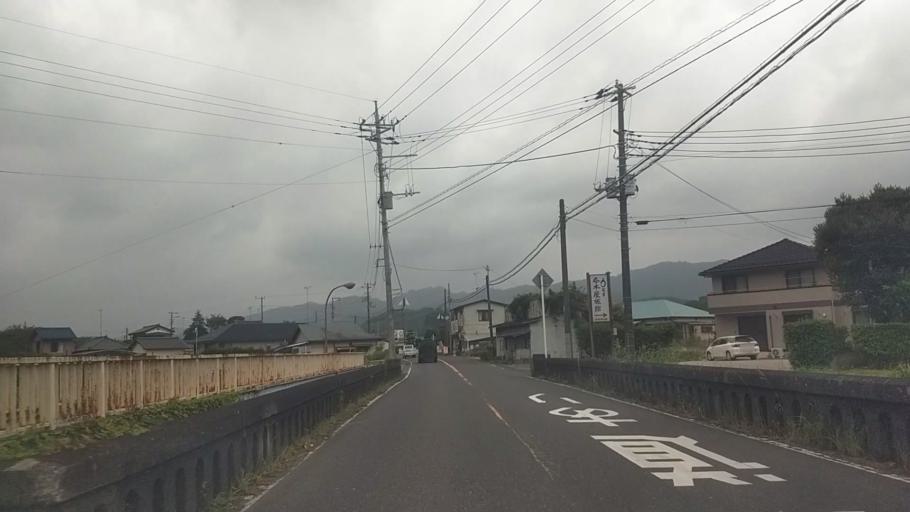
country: JP
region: Chiba
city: Kawaguchi
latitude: 35.1328
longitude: 140.0071
